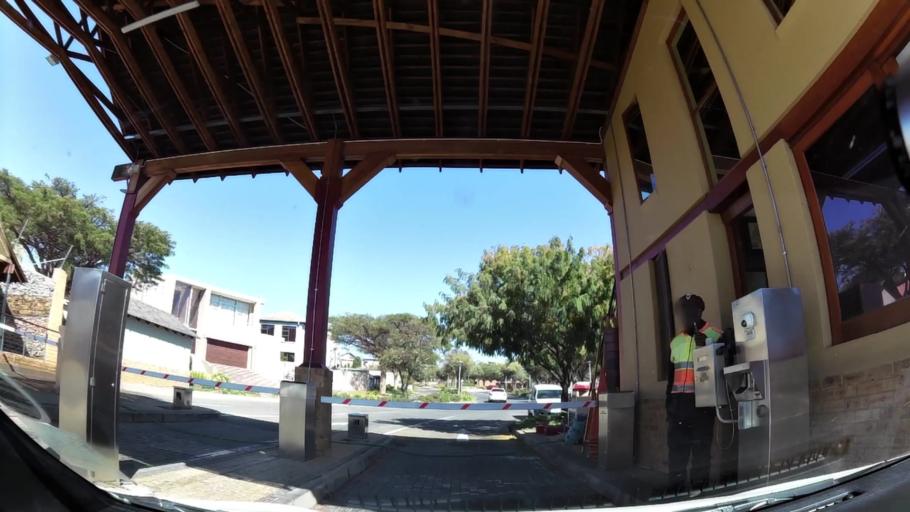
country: ZA
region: Gauteng
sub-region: City of Johannesburg Metropolitan Municipality
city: Midrand
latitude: -25.9662
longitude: 28.0989
